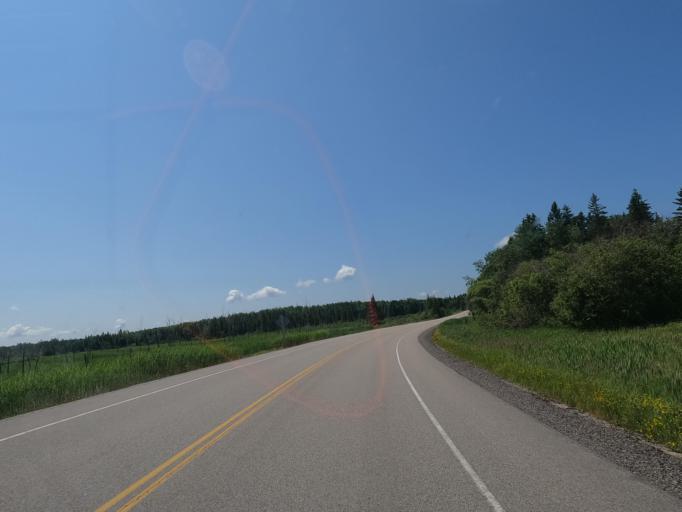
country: CA
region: Ontario
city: Dryden
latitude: 49.9046
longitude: -93.3599
